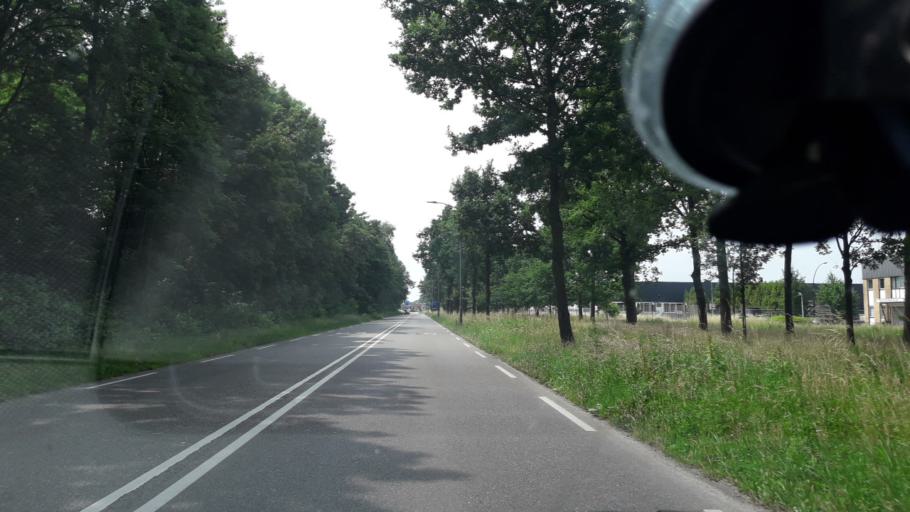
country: NL
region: Gelderland
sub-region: Gemeente Harderwijk
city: Harderwijk
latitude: 52.3557
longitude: 5.6427
